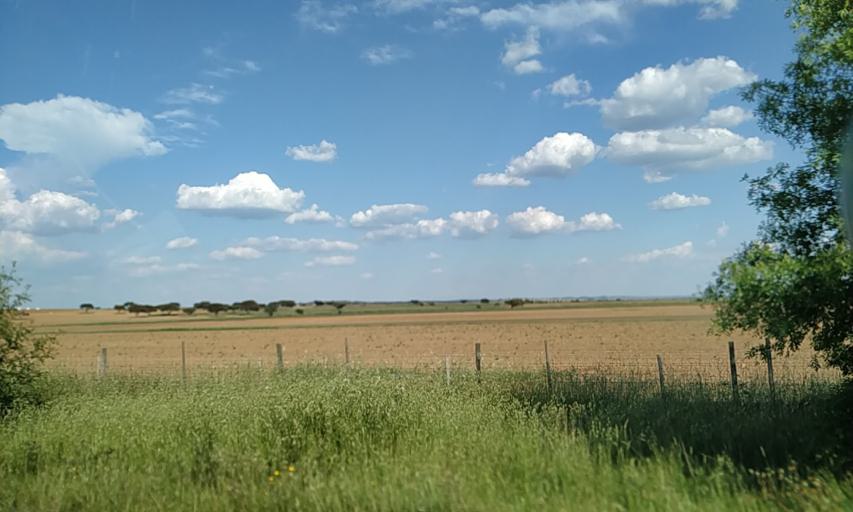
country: PT
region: Evora
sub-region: Estremoz
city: Estremoz
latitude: 38.9765
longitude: -7.4872
